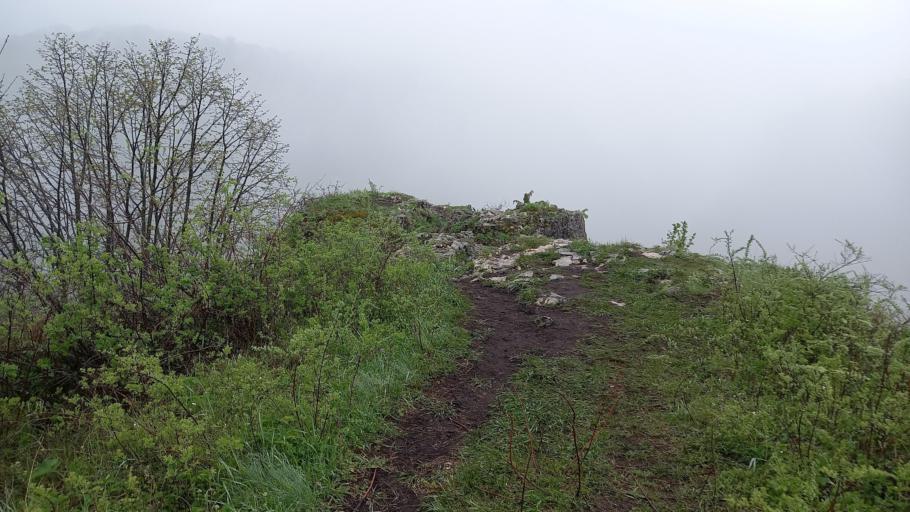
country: RU
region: Kabardino-Balkariya
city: Gundelen
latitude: 43.5906
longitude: 43.1201
